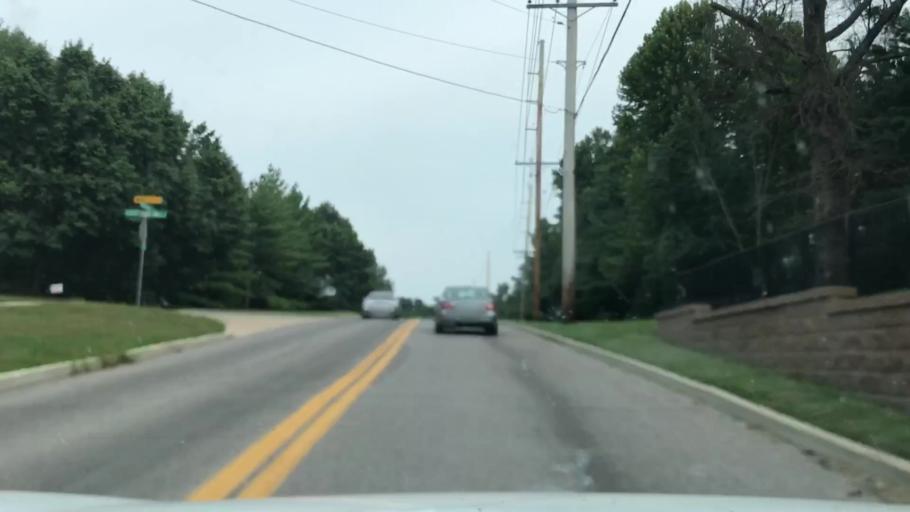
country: US
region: Missouri
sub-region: Saint Louis County
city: Chesterfield
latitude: 38.6551
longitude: -90.6181
